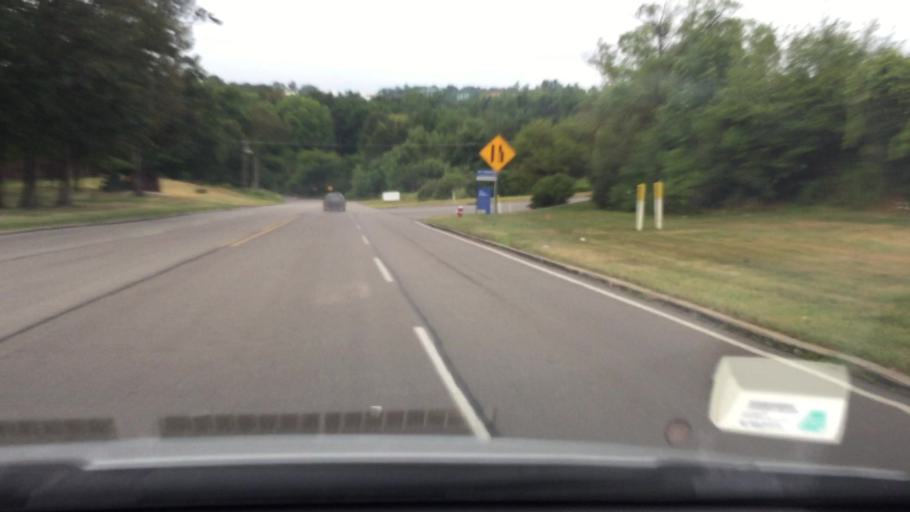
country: US
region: Pennsylvania
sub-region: Butler County
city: Cranberry Township
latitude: 40.6650
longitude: -80.1009
